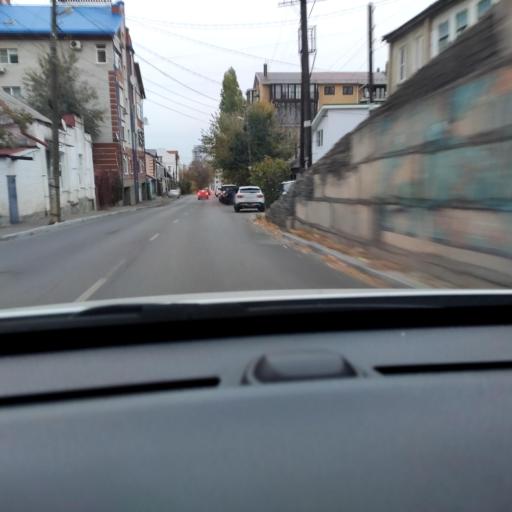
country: RU
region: Voronezj
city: Voronezh
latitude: 51.6678
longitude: 39.2149
